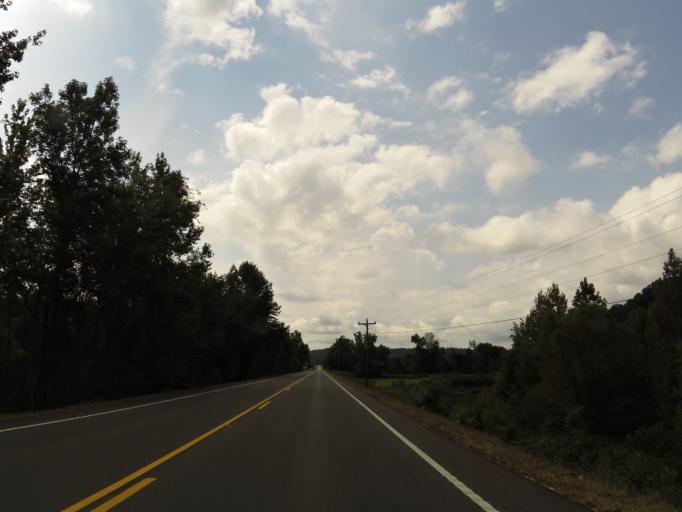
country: US
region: Tennessee
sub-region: Perry County
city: Linden
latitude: 35.7503
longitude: -87.8089
